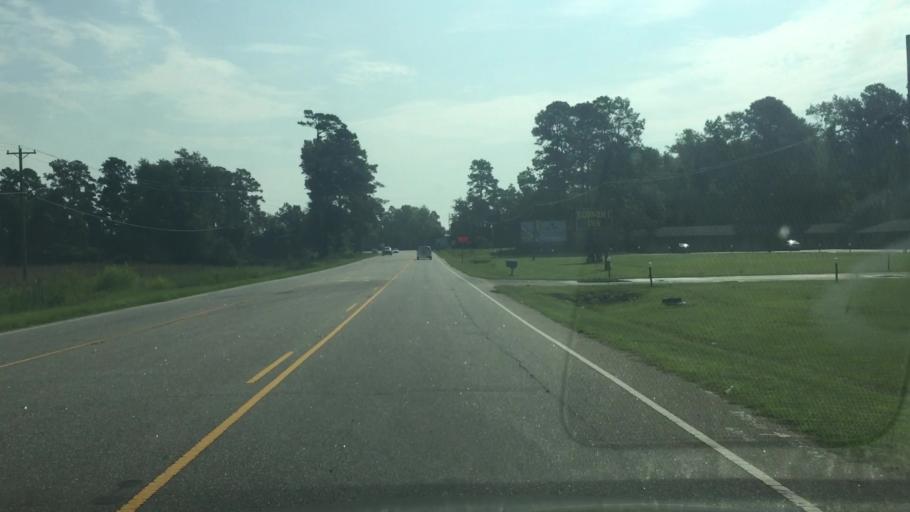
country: US
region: North Carolina
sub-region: Columbus County
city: Tabor City
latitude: 34.1587
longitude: -78.8535
